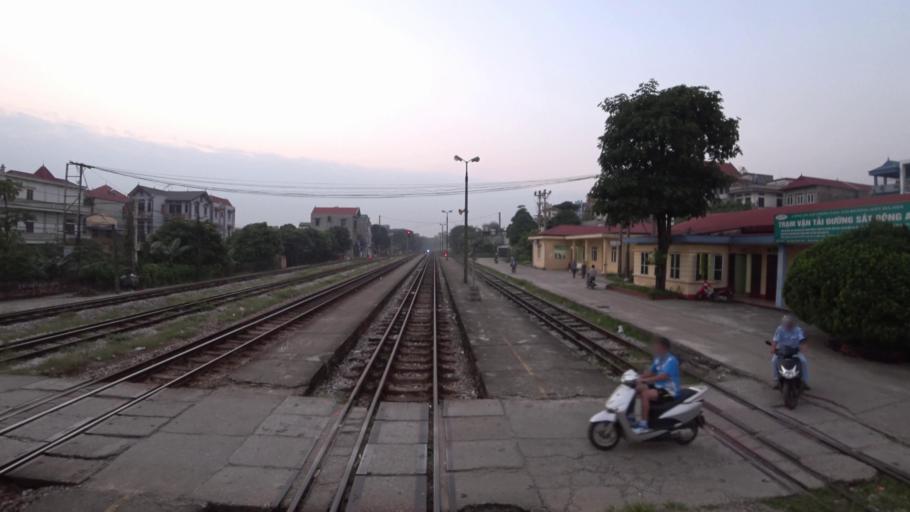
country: VN
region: Ha Noi
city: Soc Son
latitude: 21.2183
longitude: 105.8593
